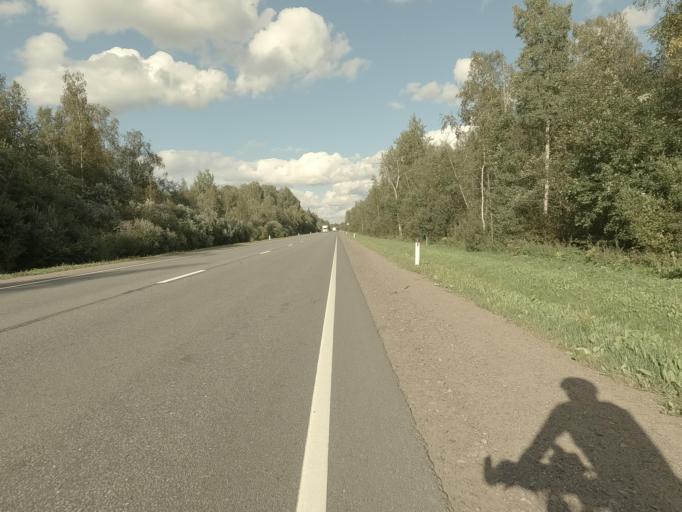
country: RU
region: Leningrad
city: Nikol'skoye
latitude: 59.6564
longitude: 30.8633
